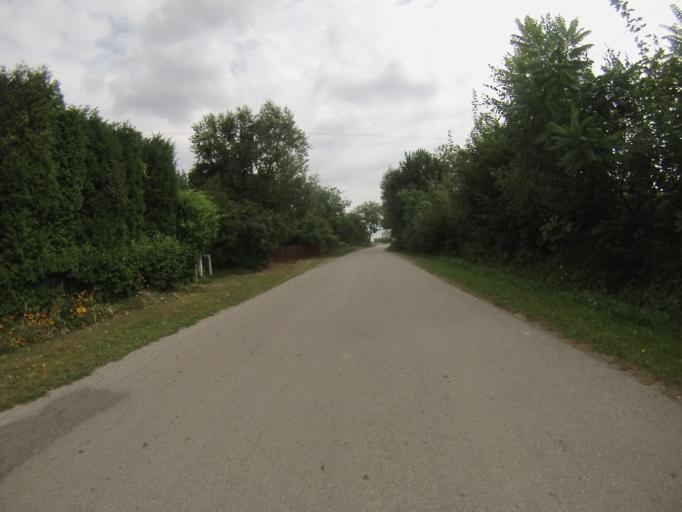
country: PL
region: Swietokrzyskie
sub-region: Powiat kielecki
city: Lagow
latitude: 50.7199
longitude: 21.1170
